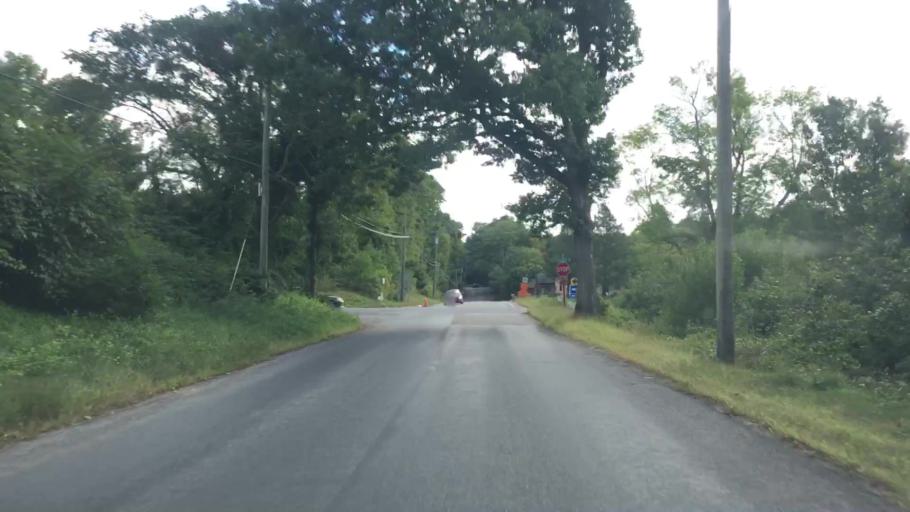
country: US
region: Connecticut
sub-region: Tolland County
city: Stafford Springs
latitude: 41.9175
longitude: -72.1925
